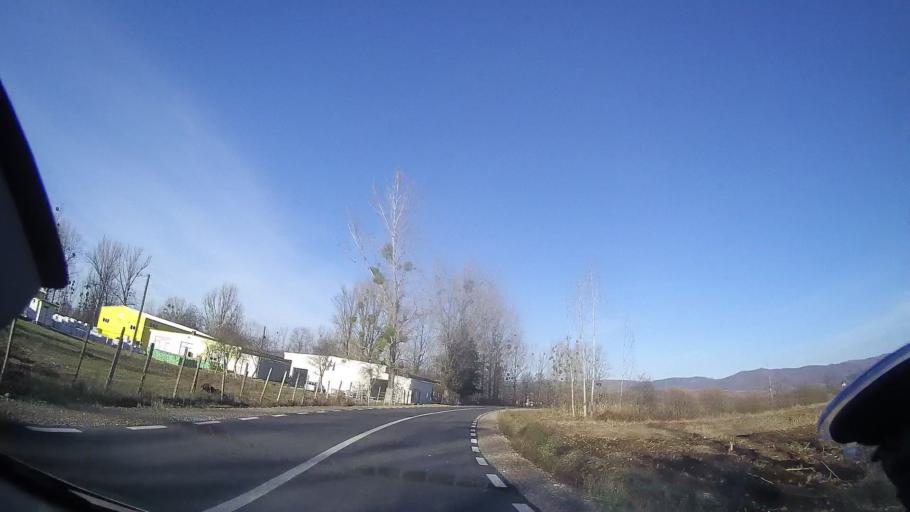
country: RO
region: Bihor
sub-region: Comuna Vadu Crisului
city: Vadu Crisului
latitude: 47.0047
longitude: 22.5012
